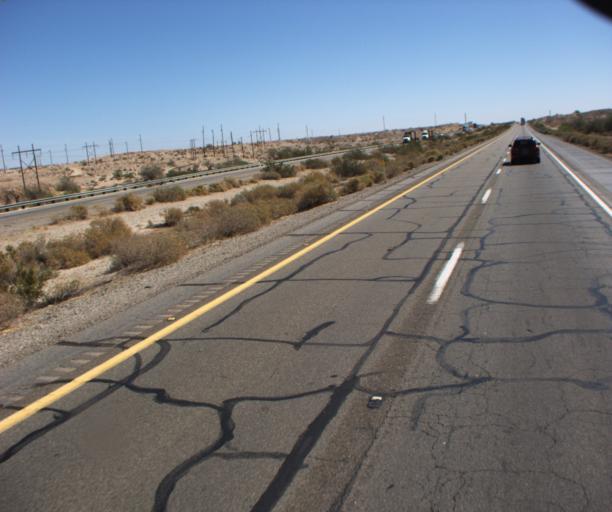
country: US
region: Arizona
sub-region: Yuma County
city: Wellton
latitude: 32.6635
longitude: -114.2697
